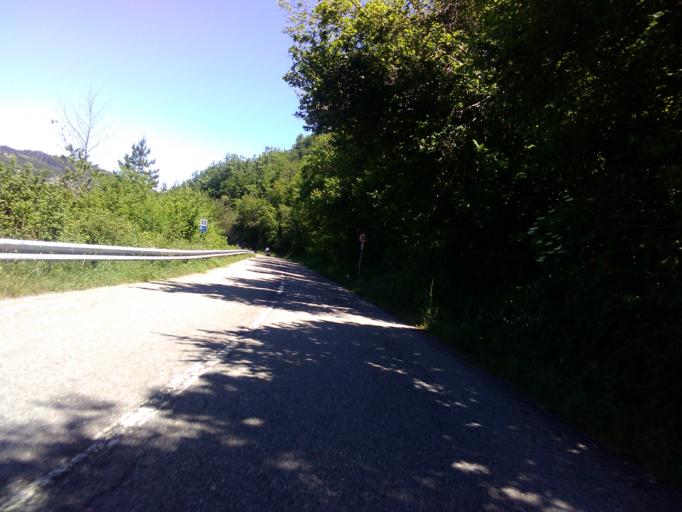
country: IT
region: Emilia-Romagna
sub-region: Provincia di Parma
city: Terenzo
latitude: 44.5744
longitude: 10.0590
